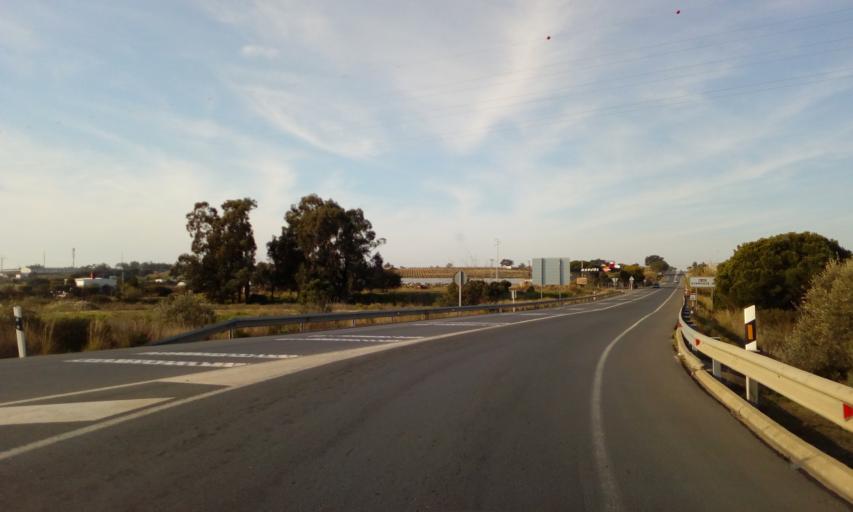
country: ES
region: Andalusia
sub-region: Provincia de Huelva
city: Lepe
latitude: 37.2538
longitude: -7.2337
